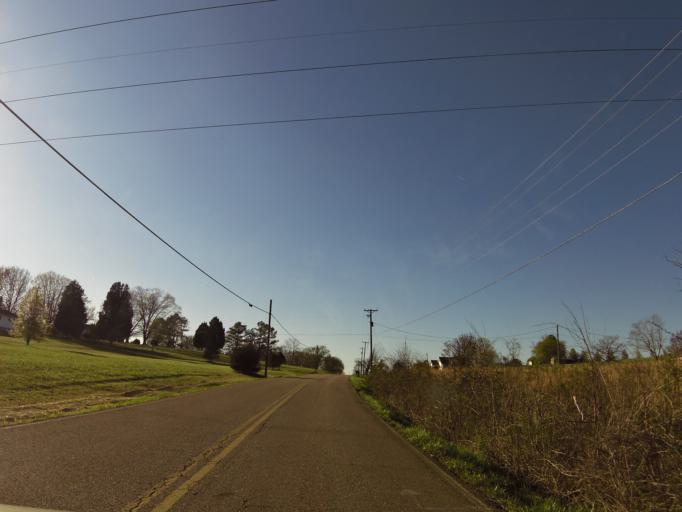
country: US
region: Tennessee
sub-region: Sevier County
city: Seymour
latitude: 35.9607
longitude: -83.7825
